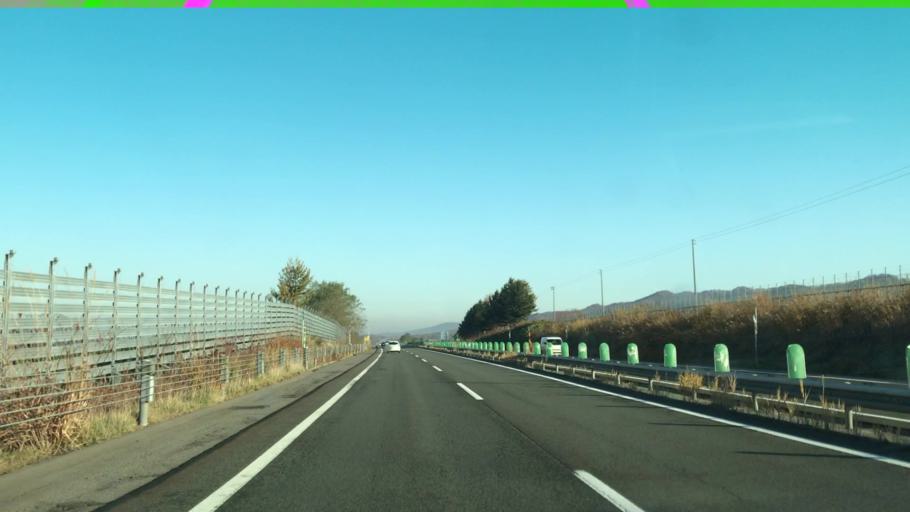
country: JP
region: Hokkaido
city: Sunagawa
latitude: 43.4340
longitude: 141.9151
